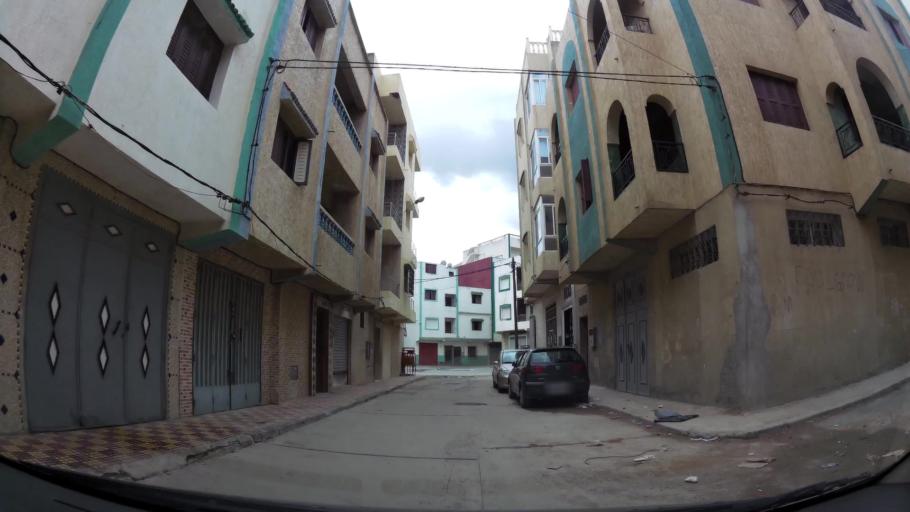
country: MA
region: Tanger-Tetouan
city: Tetouan
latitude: 35.5632
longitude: -5.3481
